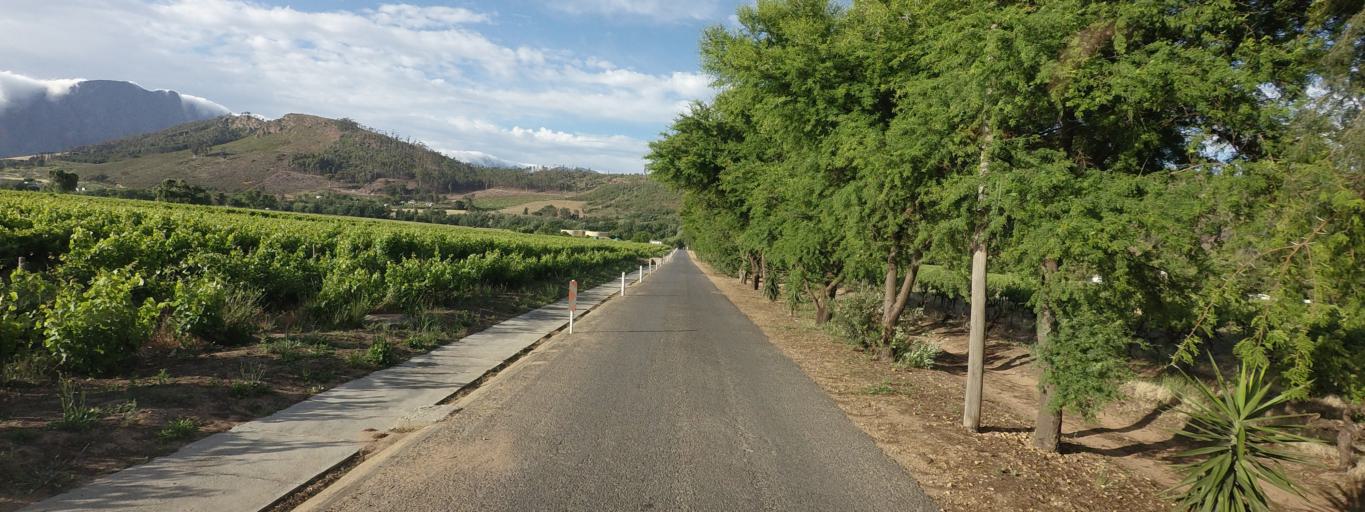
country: ZA
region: Western Cape
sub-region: Cape Winelands District Municipality
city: Paarl
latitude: -33.8947
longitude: 19.0966
